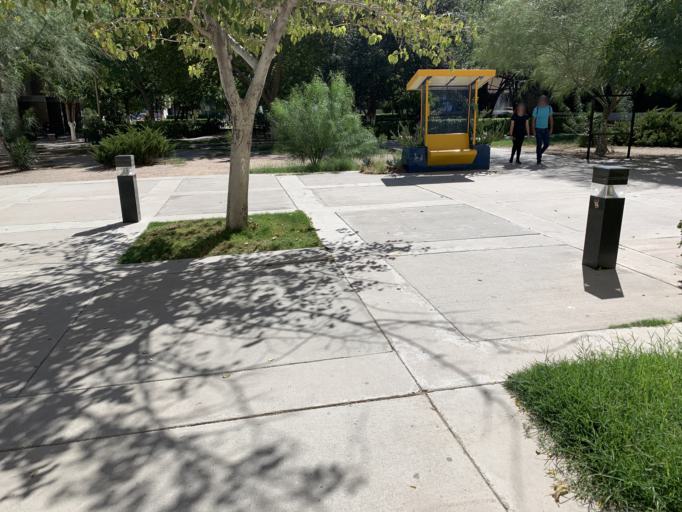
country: MX
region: Chihuahua
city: Ciudad Juarez
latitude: 31.7437
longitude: -106.4321
